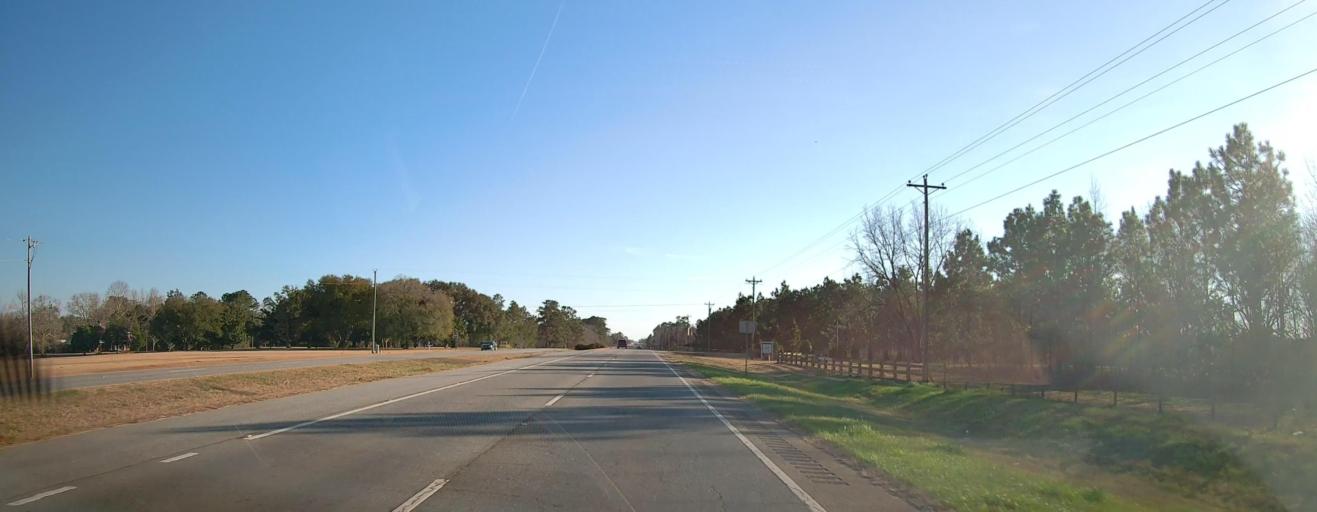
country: US
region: Georgia
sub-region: Lee County
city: Leesburg
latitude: 31.7114
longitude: -84.1726
